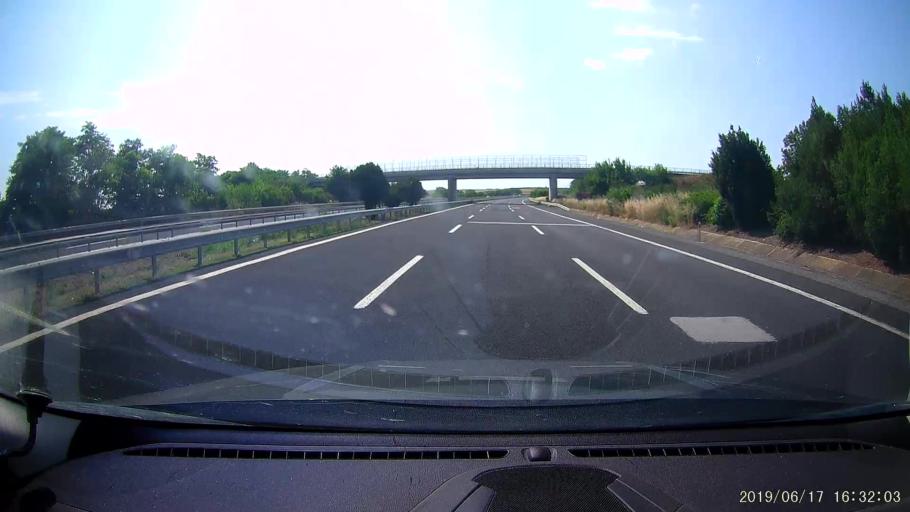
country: TR
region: Kirklareli
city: Buyukkaristiran
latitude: 41.3649
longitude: 27.6098
